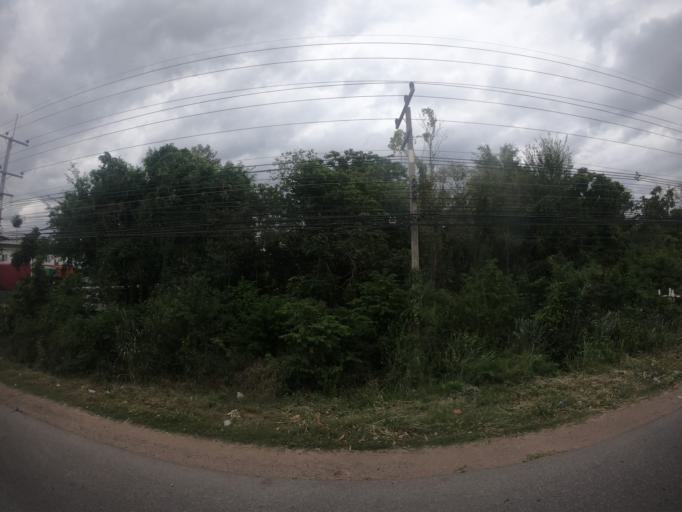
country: TH
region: Nakhon Ratchasima
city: Nakhon Ratchasima
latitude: 14.9065
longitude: 102.1554
